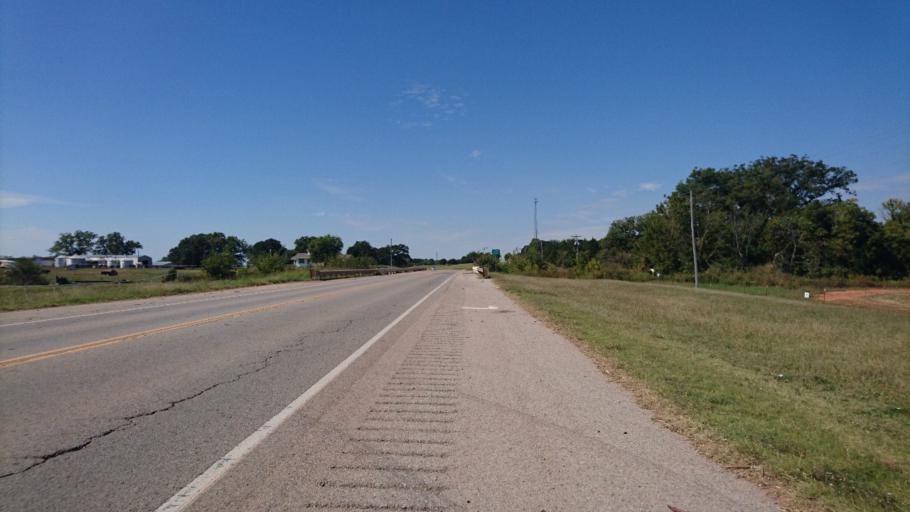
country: US
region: Oklahoma
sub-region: Oklahoma County
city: Jones
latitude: 35.6670
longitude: -97.3128
